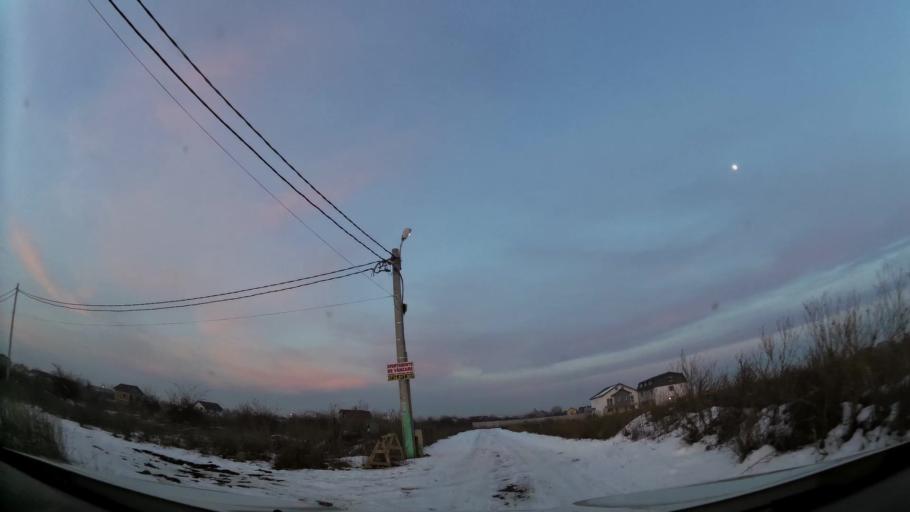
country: RO
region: Ilfov
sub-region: Comuna Magurele
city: Magurele
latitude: 44.3869
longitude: 26.0285
